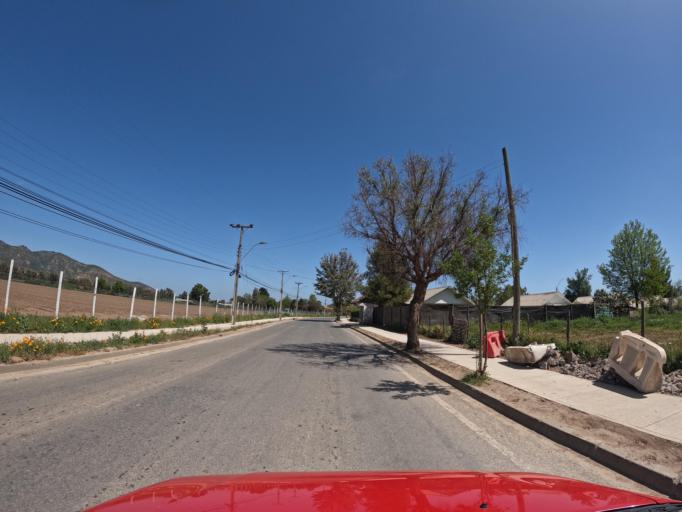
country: CL
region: O'Higgins
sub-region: Provincia de Colchagua
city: Santa Cruz
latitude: -34.7275
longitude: -71.6591
